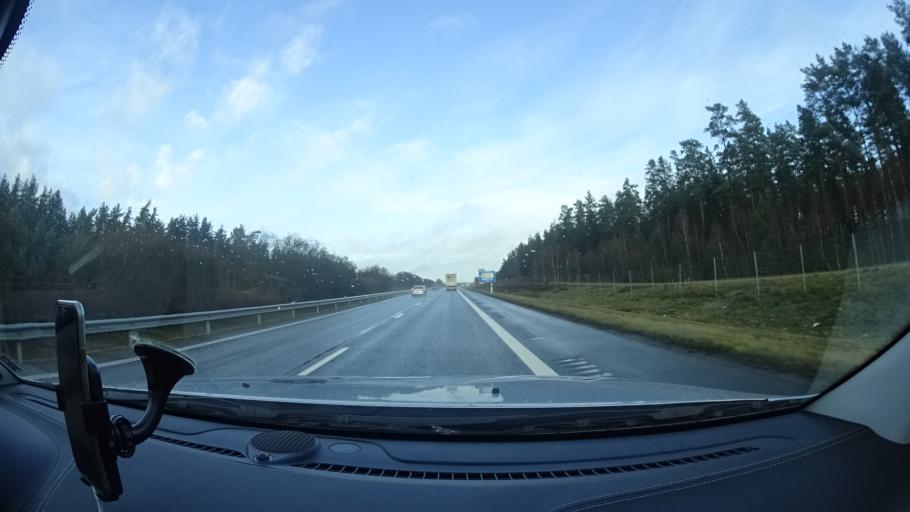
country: SE
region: Joenkoeping
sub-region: Vaggeryds Kommun
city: Skillingaryd
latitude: 57.4425
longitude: 14.1002
